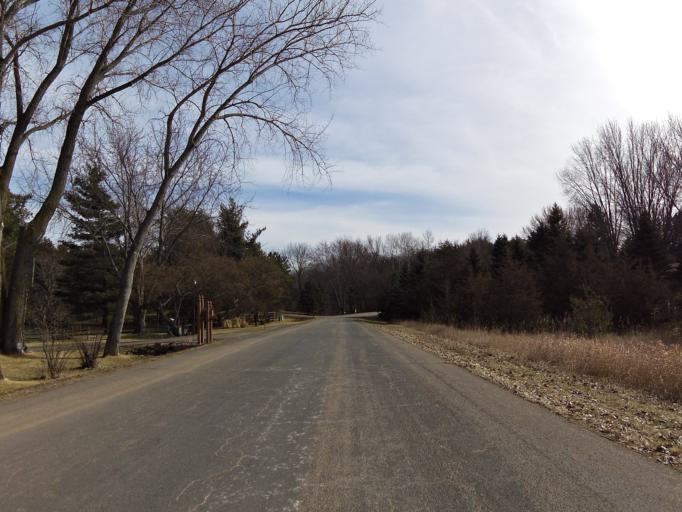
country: US
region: Minnesota
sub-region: Washington County
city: Lakeland
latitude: 44.9465
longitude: -92.7833
